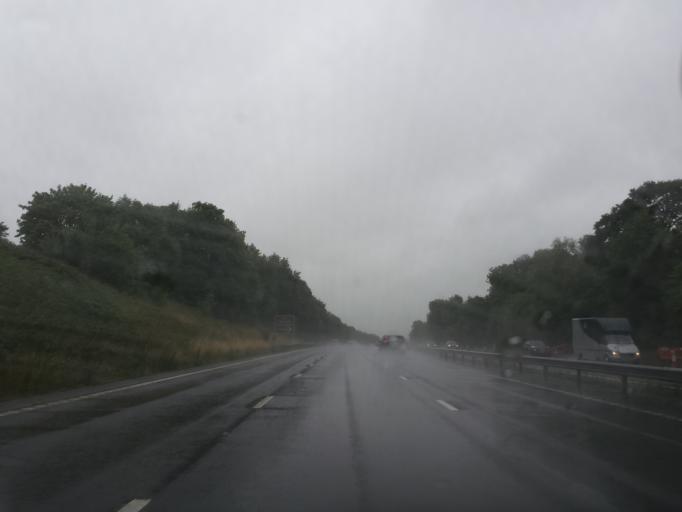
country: GB
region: England
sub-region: Coventry
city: Coventry
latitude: 52.3711
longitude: -1.5110
